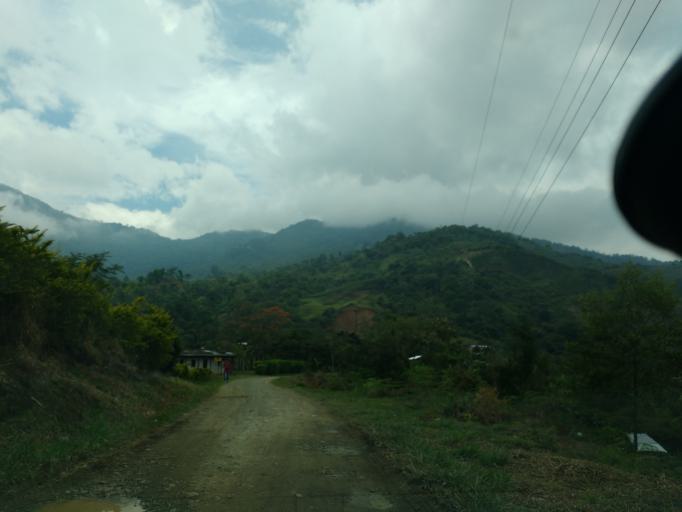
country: CO
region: Cauca
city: Santander de Quilichao
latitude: 2.9192
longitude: -76.4701
